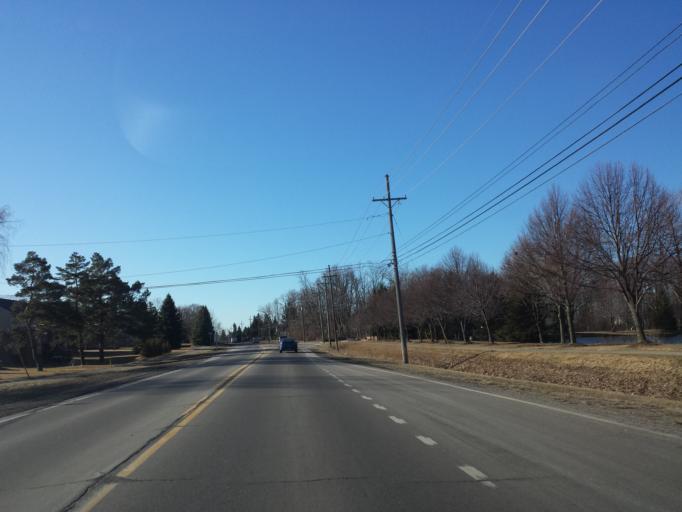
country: US
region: Michigan
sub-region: Oakland County
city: Troy
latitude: 42.6306
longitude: -83.1519
